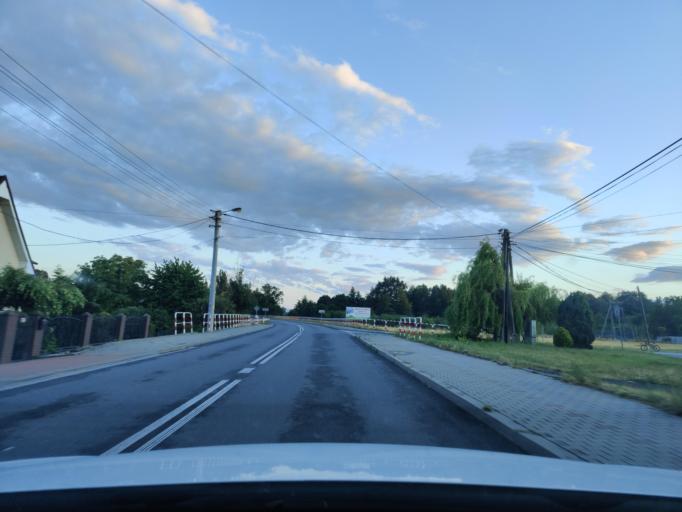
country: PL
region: Opole Voivodeship
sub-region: Powiat nyski
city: Chroscina
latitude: 50.6490
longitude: 17.3837
